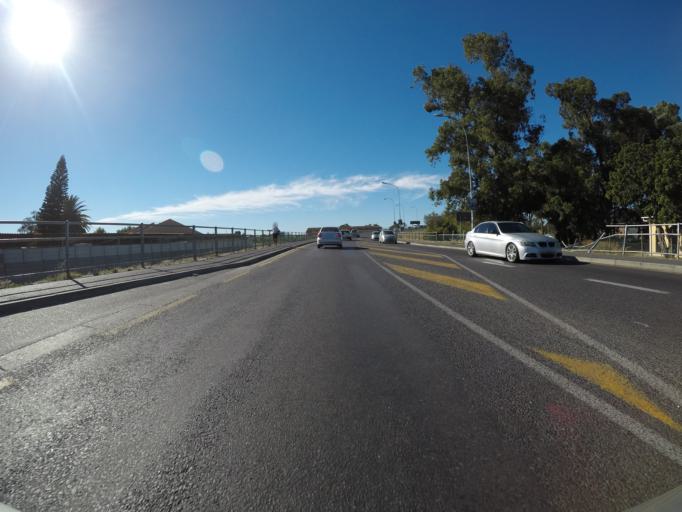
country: ZA
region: Western Cape
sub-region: City of Cape Town
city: Kraaifontein
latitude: -33.9339
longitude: 18.6760
